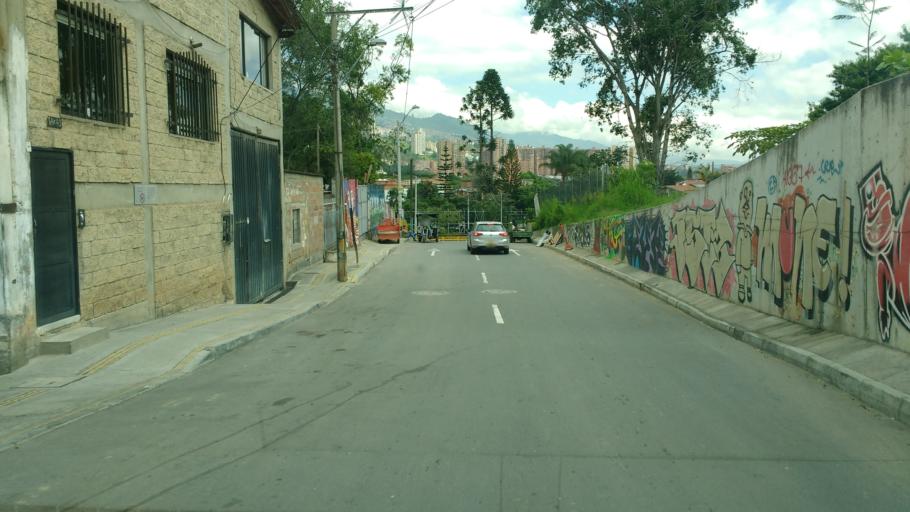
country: CO
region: Antioquia
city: Medellin
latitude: 6.2553
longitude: -75.6079
